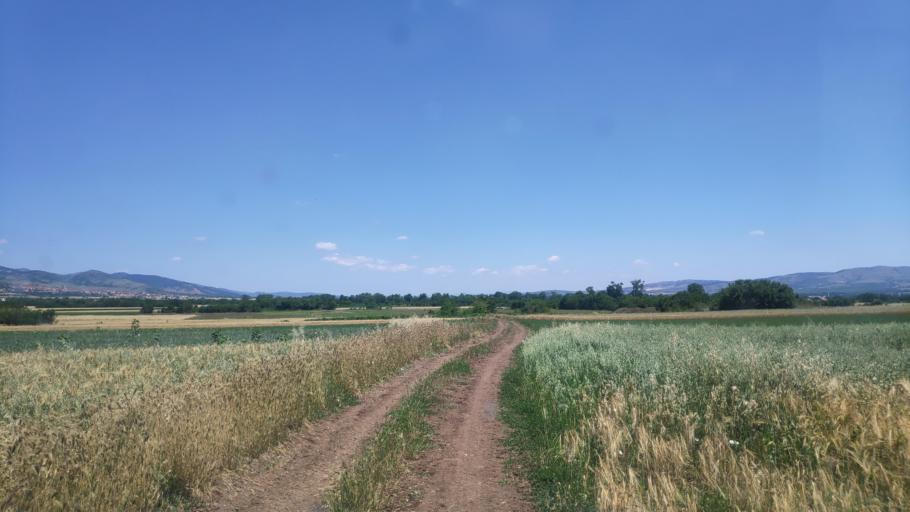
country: MK
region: Kumanovo
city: Bedinje
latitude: 42.1662
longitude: 21.6843
